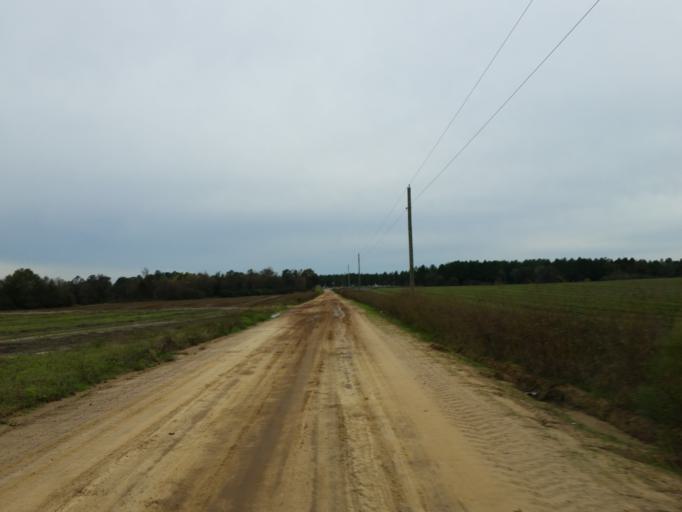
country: US
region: Georgia
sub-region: Crisp County
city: Cordele
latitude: 31.8582
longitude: -83.7396
